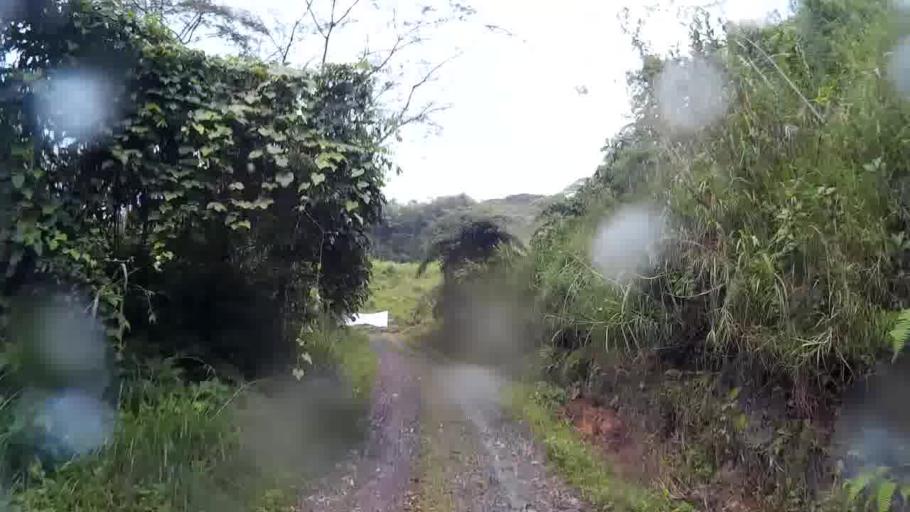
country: CO
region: Quindio
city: Filandia
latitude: 4.7105
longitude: -75.6817
